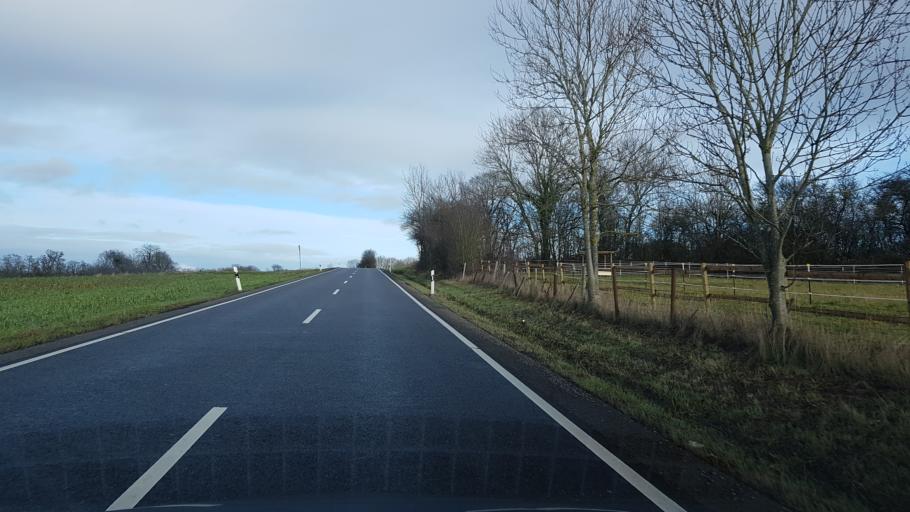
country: DE
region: Saarland
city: Sankt Ingbert
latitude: 49.2247
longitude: 7.1182
